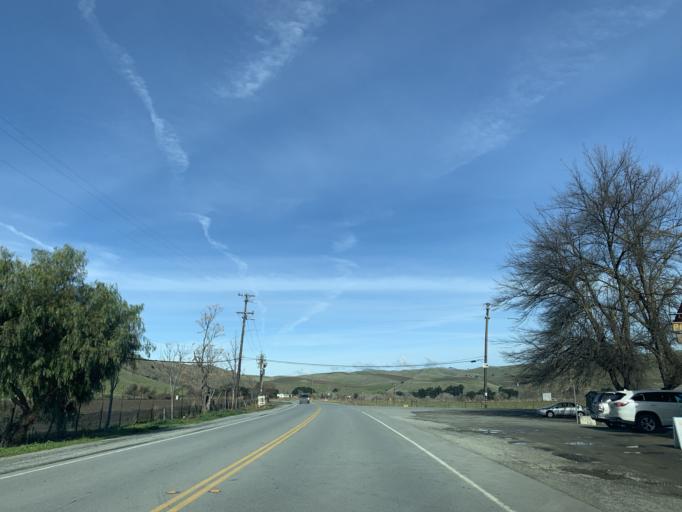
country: US
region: California
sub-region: San Benito County
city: Ridgemark
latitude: 36.7281
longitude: -121.2789
